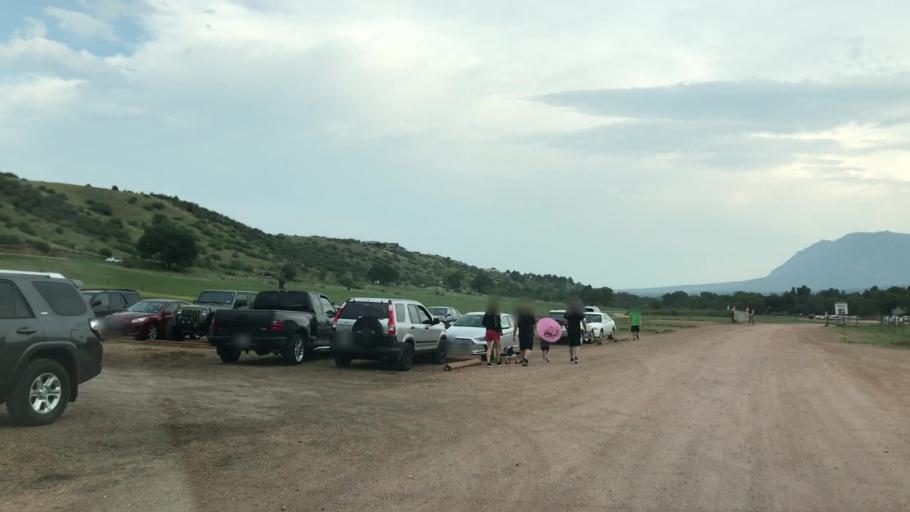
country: US
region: Colorado
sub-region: El Paso County
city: Manitou Springs
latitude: 38.8766
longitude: -104.8713
